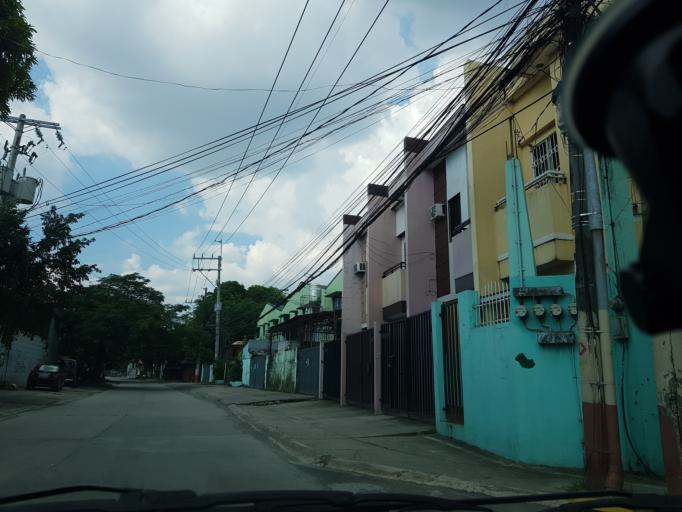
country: PH
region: Metro Manila
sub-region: Pasig
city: Pasig City
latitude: 14.5844
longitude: 121.0913
